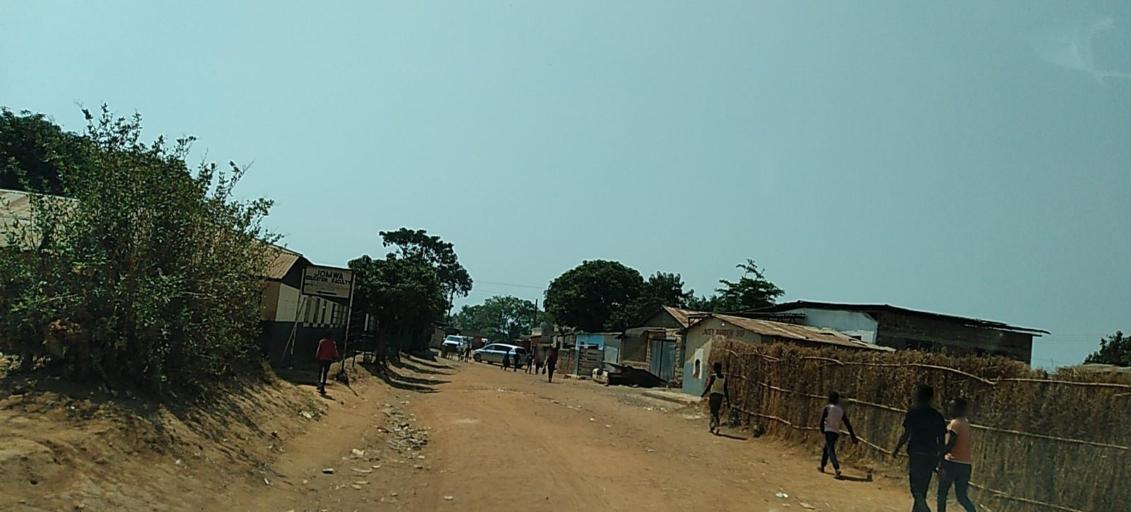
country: ZM
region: Copperbelt
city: Luanshya
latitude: -13.3550
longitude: 28.4150
